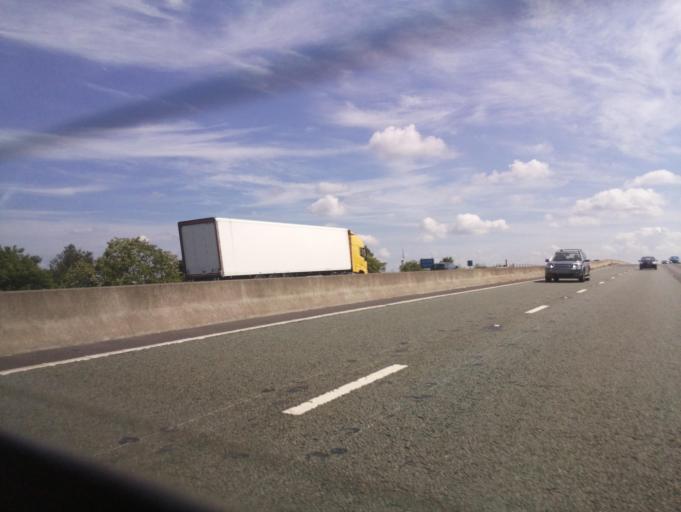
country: GB
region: England
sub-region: North Lincolnshire
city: Gunness
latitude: 53.5563
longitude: -0.7494
